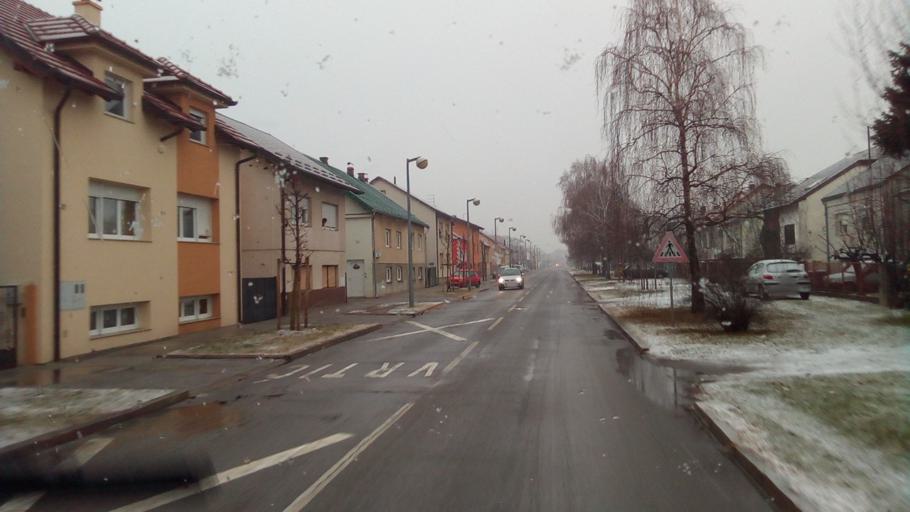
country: HR
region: Varazdinska
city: Varazdin
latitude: 46.2998
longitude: 16.3207
